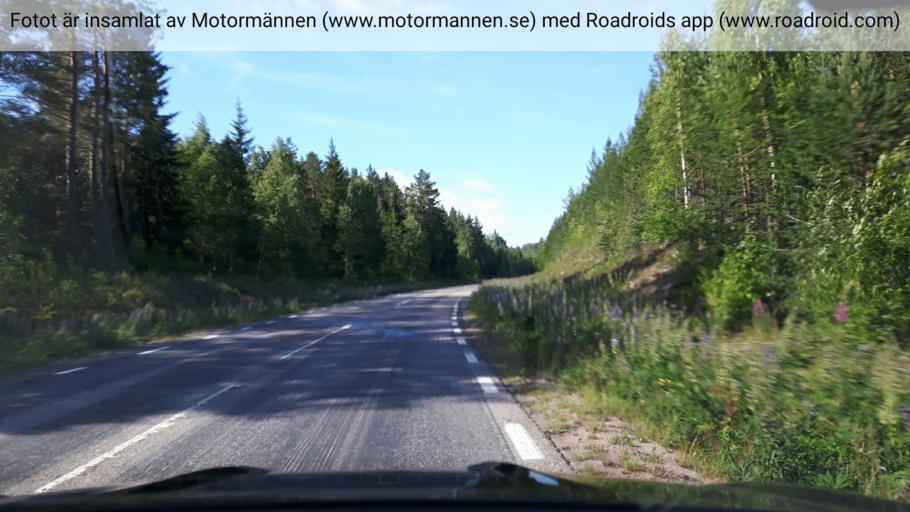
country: SE
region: Gaevleborg
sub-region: Ljusdals Kommun
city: Farila
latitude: 61.7784
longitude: 15.5966
